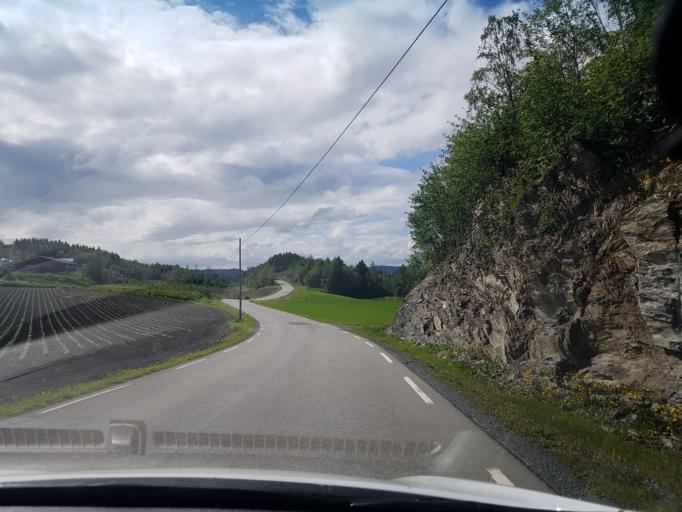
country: NO
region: Nord-Trondelag
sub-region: Stjordal
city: Stjordalshalsen
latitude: 63.5905
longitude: 11.0010
